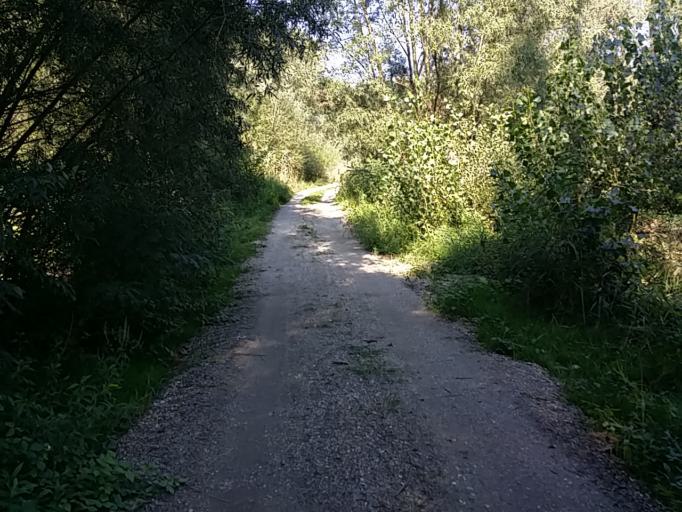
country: HR
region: Koprivnicko-Krizevacka
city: Ferdinandovac
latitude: 46.1160
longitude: 17.2122
